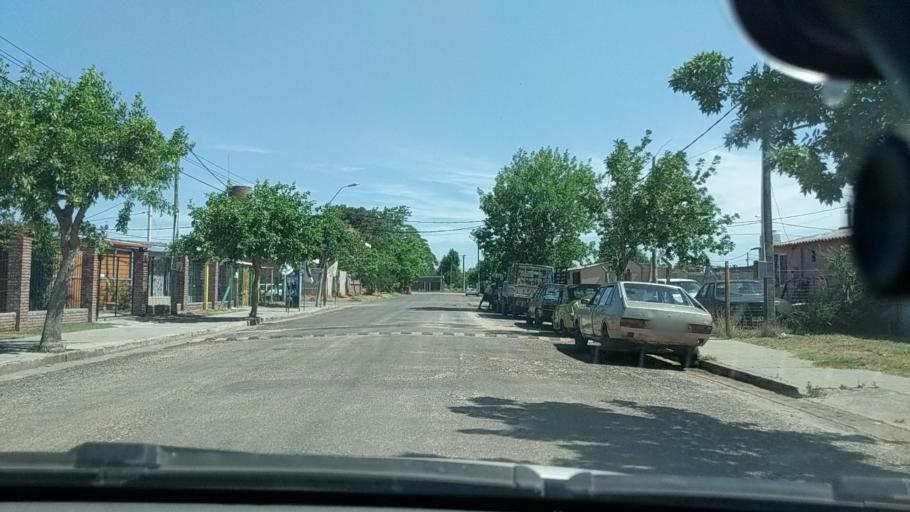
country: UY
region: Tacuarembo
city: Paso de los Toros
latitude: -32.8088
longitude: -56.5304
